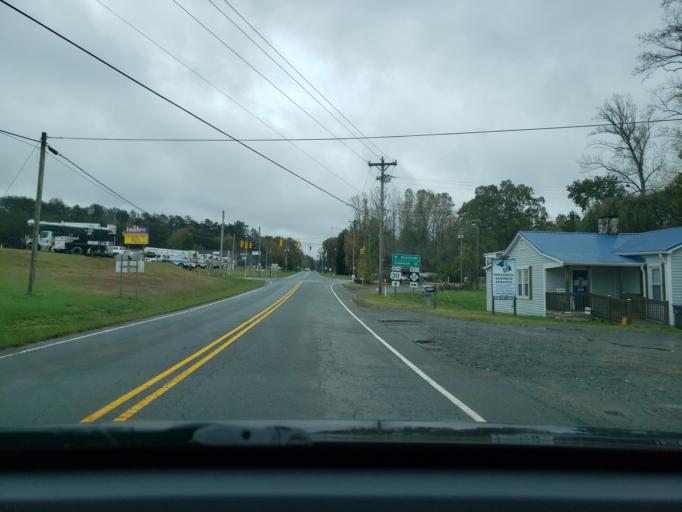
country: US
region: North Carolina
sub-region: Stokes County
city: Walnut Cove
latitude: 36.2816
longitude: -80.1456
